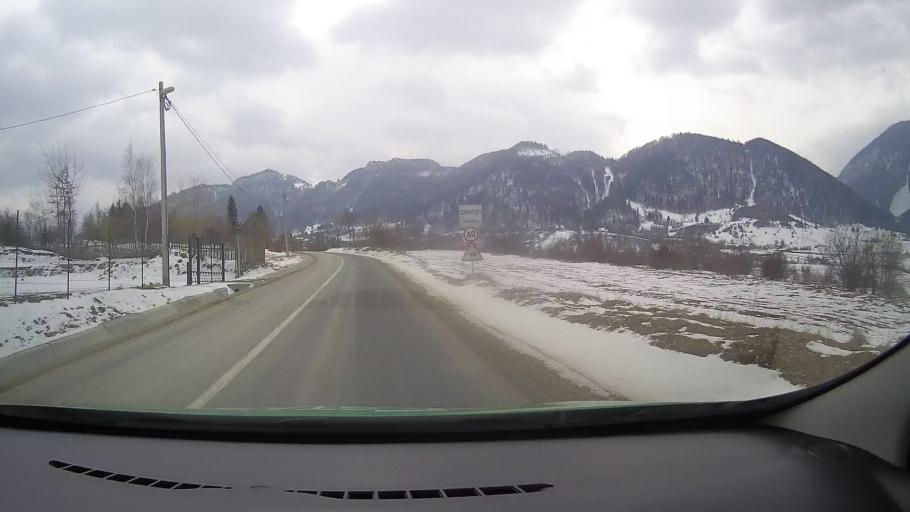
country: RO
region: Brasov
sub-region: Comuna Zarnesti
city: Zarnesti
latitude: 45.5492
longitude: 25.3220
